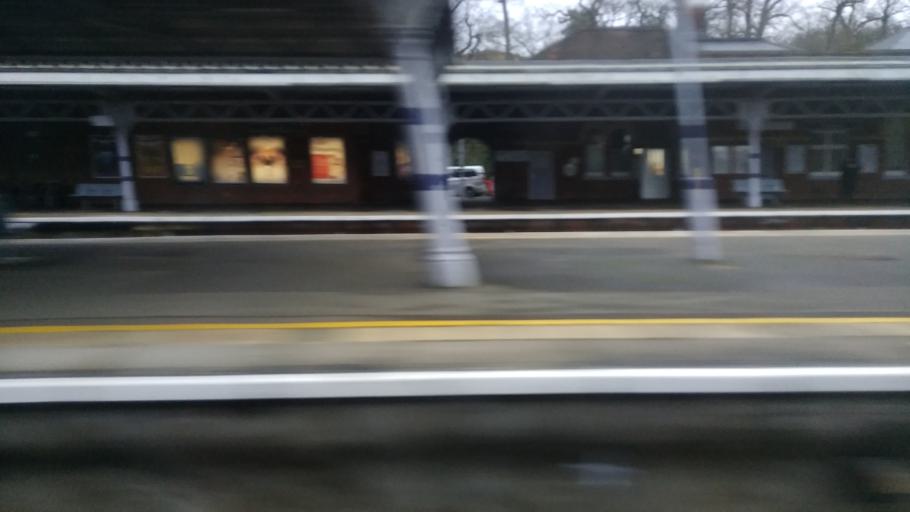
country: GB
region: England
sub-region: Greater London
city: Chislehurst
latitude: 51.4053
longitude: 0.0576
